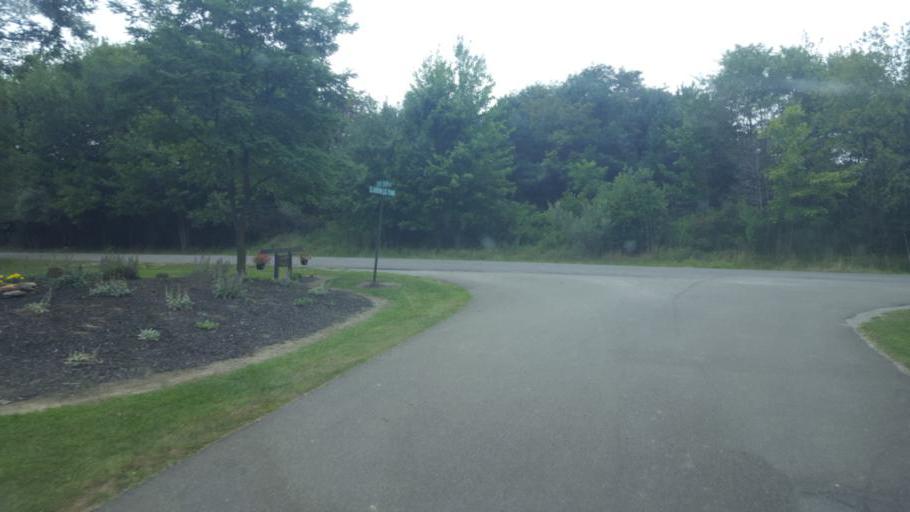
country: US
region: Pennsylvania
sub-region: Clarion County
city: Marianne
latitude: 41.2033
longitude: -79.4360
